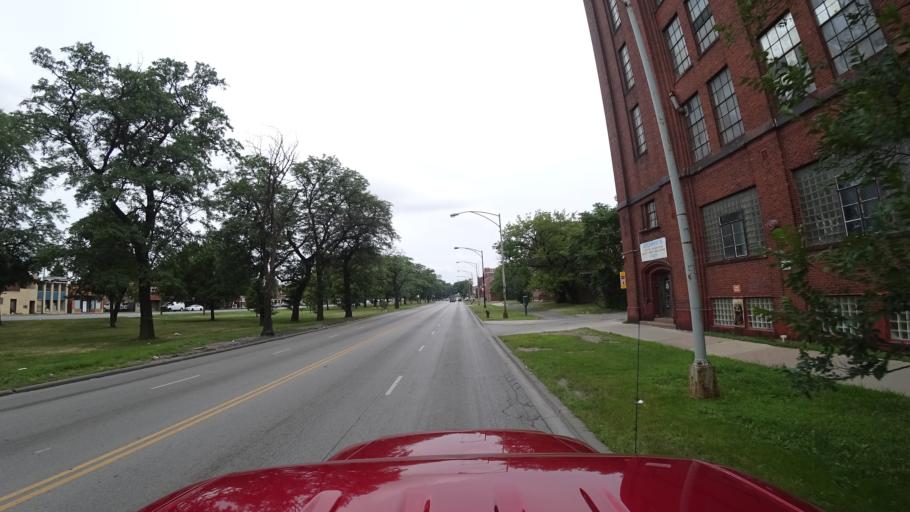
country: US
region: Illinois
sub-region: Cook County
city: Chicago
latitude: 41.8136
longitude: -87.6840
